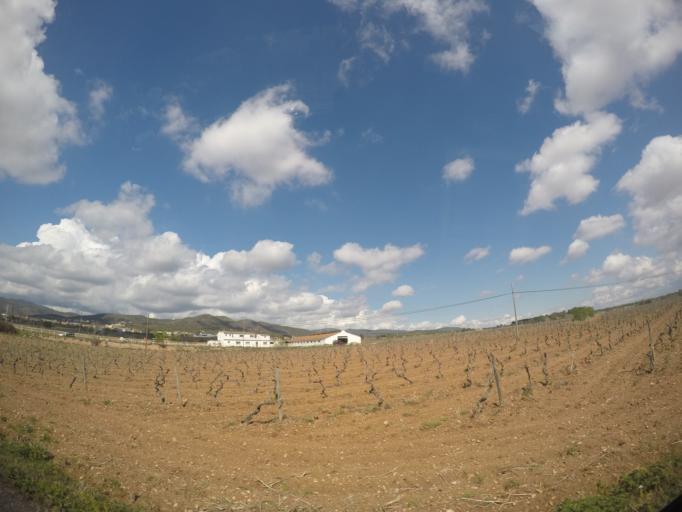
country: ES
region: Catalonia
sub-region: Provincia de Tarragona
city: Santa Oliva
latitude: 41.2839
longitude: 1.5289
